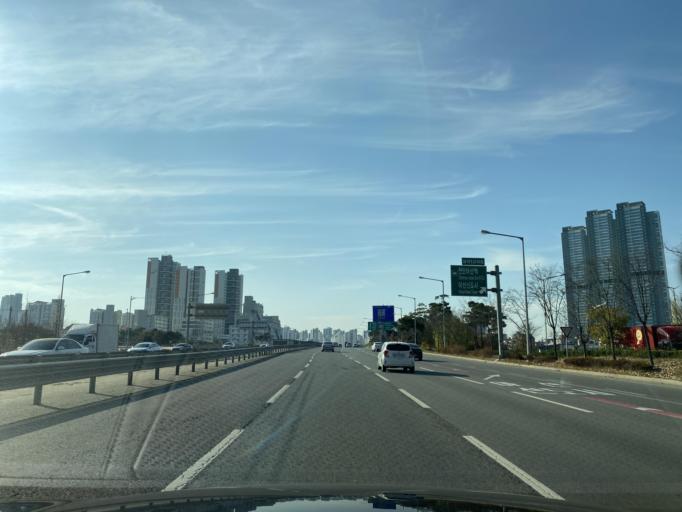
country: KR
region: Chungcheongnam-do
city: Cheonan
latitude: 36.7845
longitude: 127.1069
